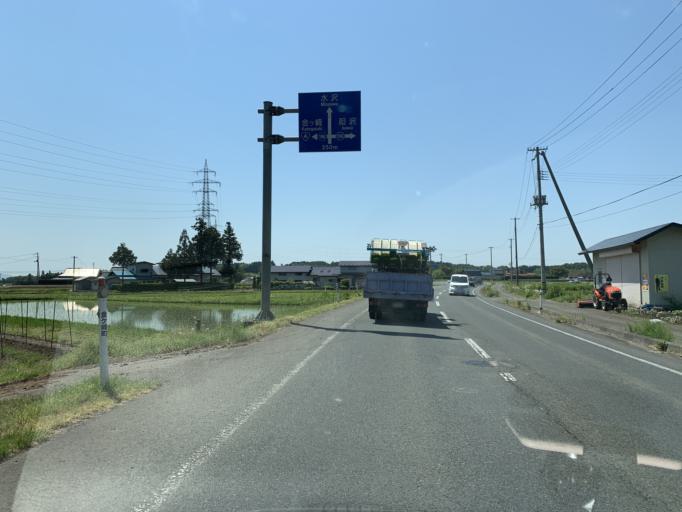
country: JP
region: Iwate
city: Mizusawa
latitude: 39.1829
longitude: 141.0785
